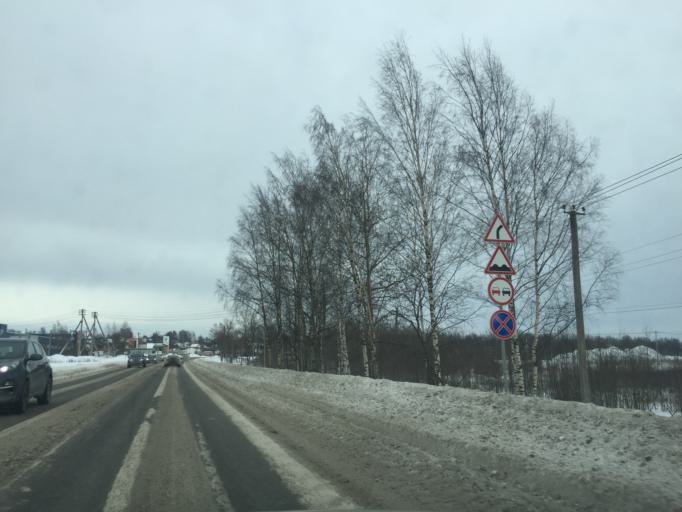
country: RU
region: Leningrad
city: Yanino Vtoroye
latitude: 59.9443
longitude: 30.5996
